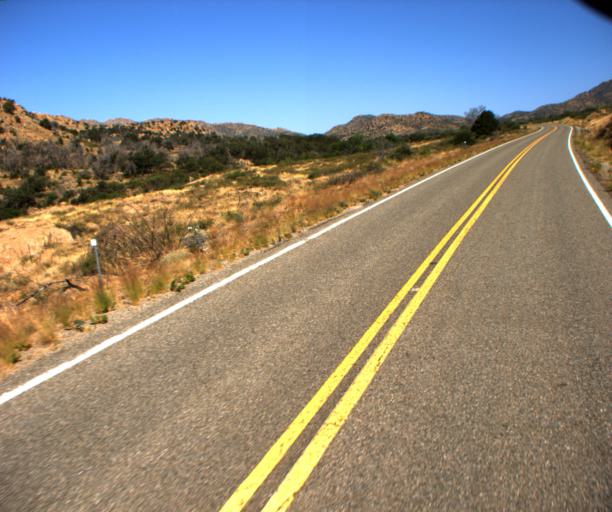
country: US
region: Arizona
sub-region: Graham County
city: Swift Trail Junction
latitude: 32.5641
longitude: -109.8012
